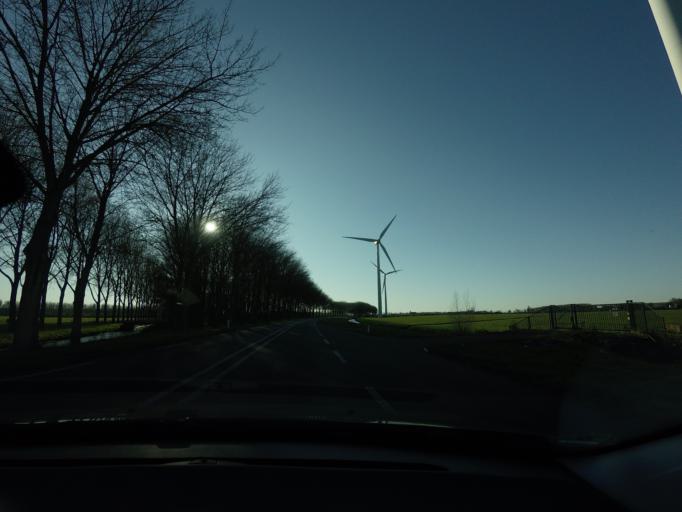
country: NL
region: Gelderland
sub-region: Gemeente Culemborg
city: Culemborg
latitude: 51.9346
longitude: 5.2000
